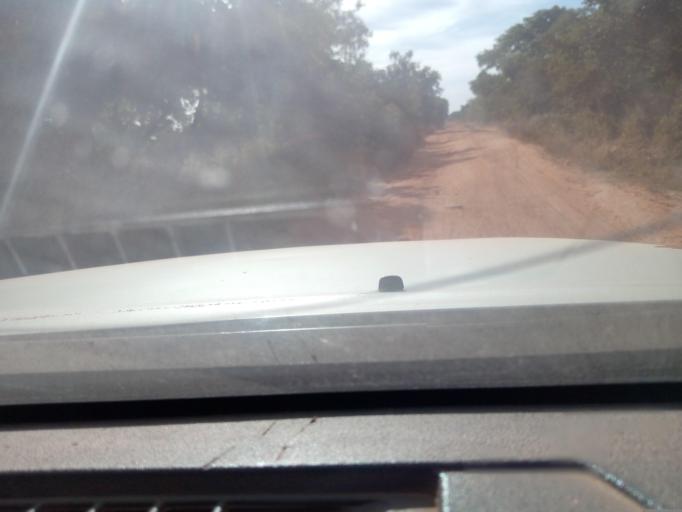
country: ML
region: Sikasso
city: Sikasso
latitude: 11.9282
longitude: -6.0711
